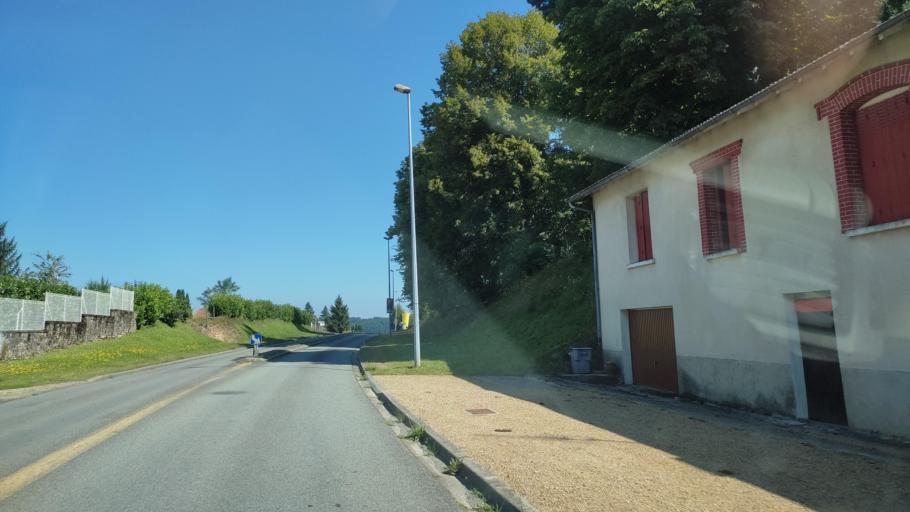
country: FR
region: Limousin
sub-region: Departement de la Haute-Vienne
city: Razes
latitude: 46.0291
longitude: 1.3446
